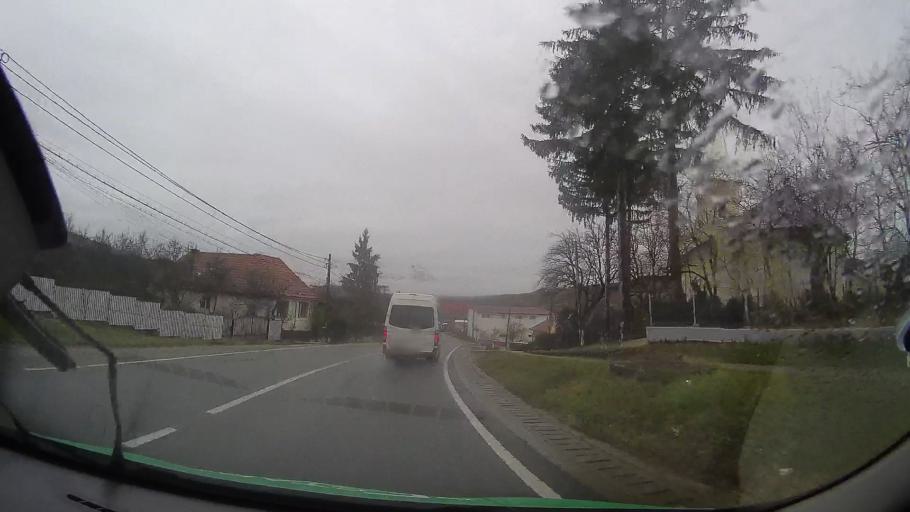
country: RO
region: Bistrita-Nasaud
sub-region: Comuna Galatii Bistritei
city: Galatii Bistritei
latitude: 47.0196
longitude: 24.4145
